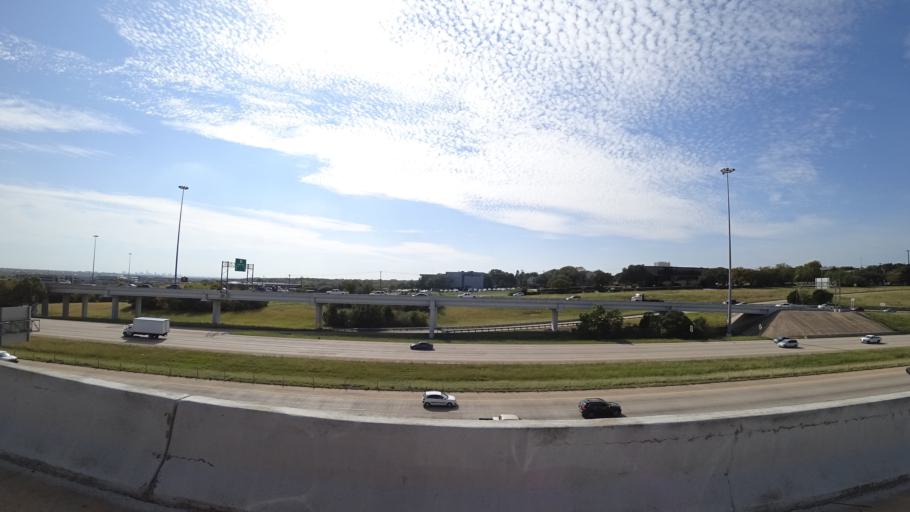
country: US
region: Texas
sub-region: Williamson County
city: Jollyville
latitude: 30.3813
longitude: -97.7395
